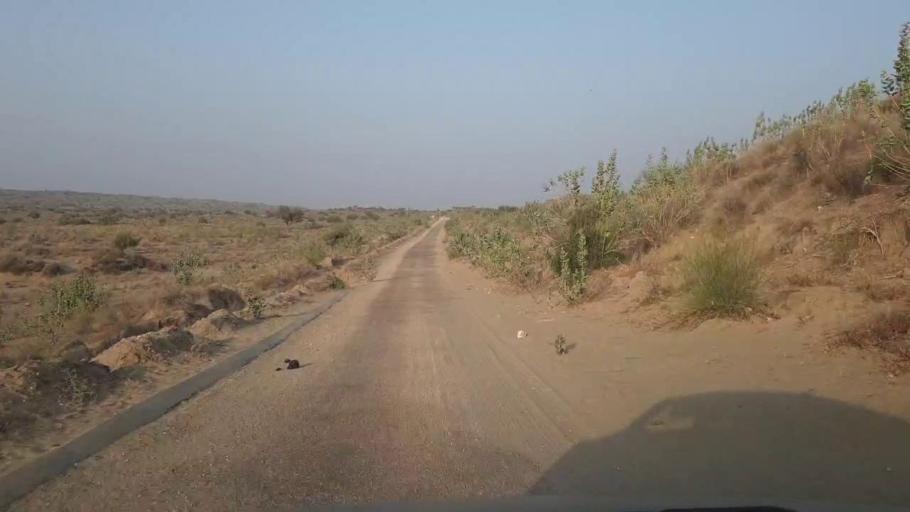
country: PK
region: Sindh
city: Umarkot
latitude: 25.2503
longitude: 69.9055
